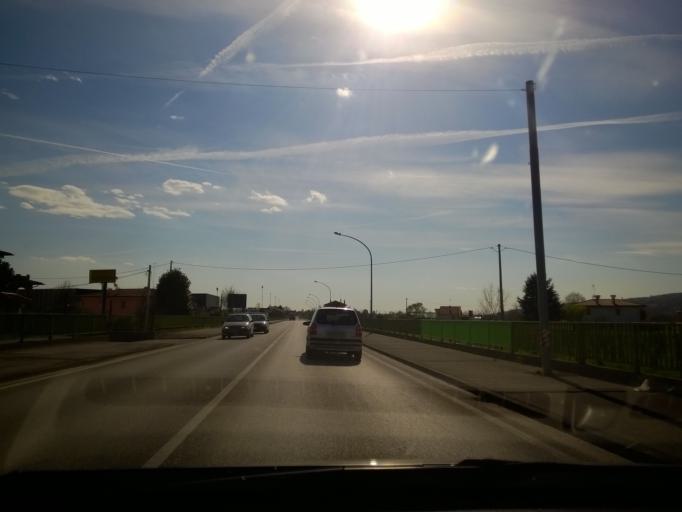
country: IT
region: Veneto
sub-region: Provincia di Treviso
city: Nervesa della Battaglia
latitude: 45.8027
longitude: 12.1852
